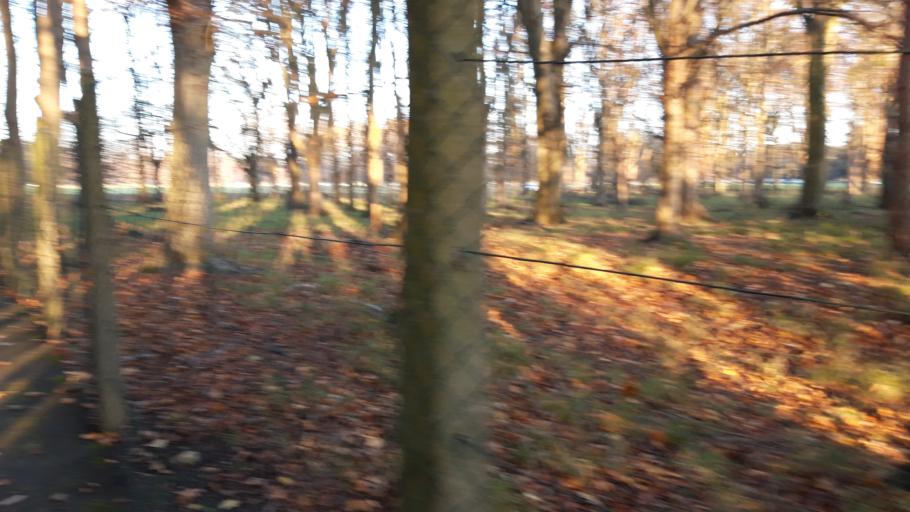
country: IE
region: Leinster
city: Chapelizod
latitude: 53.3650
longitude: -6.3481
